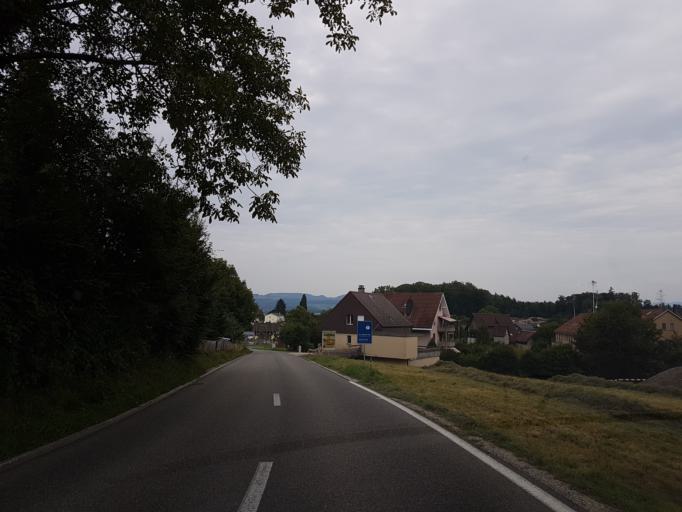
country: CH
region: Aargau
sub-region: Bezirk Muri
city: Merenschwand
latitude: 47.2476
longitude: 8.3615
